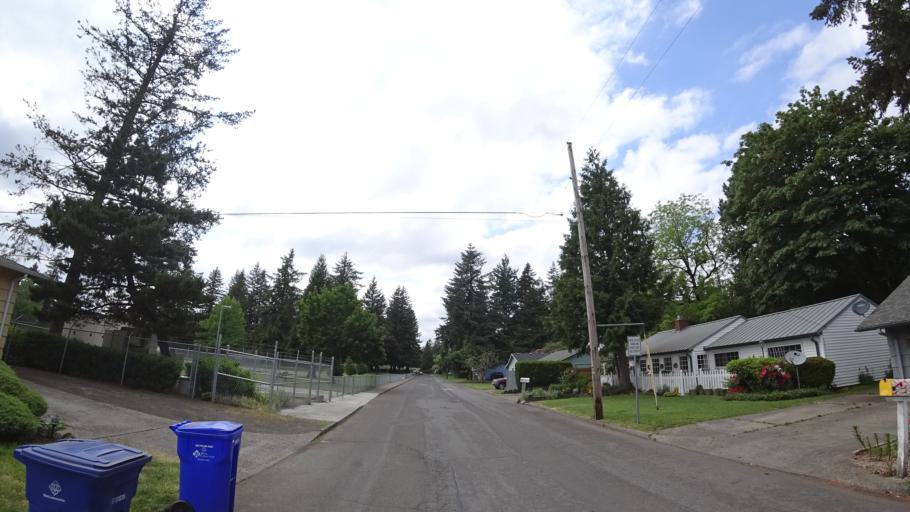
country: US
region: Oregon
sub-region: Multnomah County
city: Fairview
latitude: 45.5155
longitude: -122.4795
